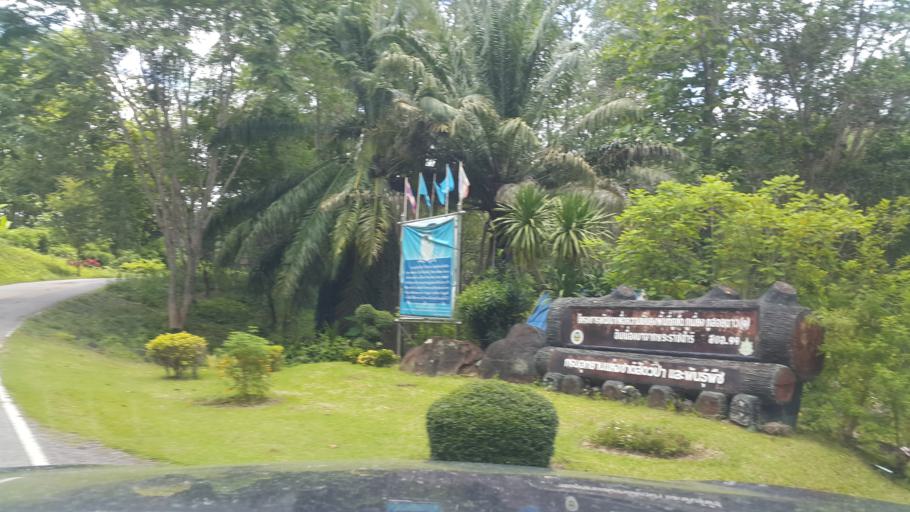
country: TH
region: Loei
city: Na Haeo
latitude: 17.6273
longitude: 100.8936
